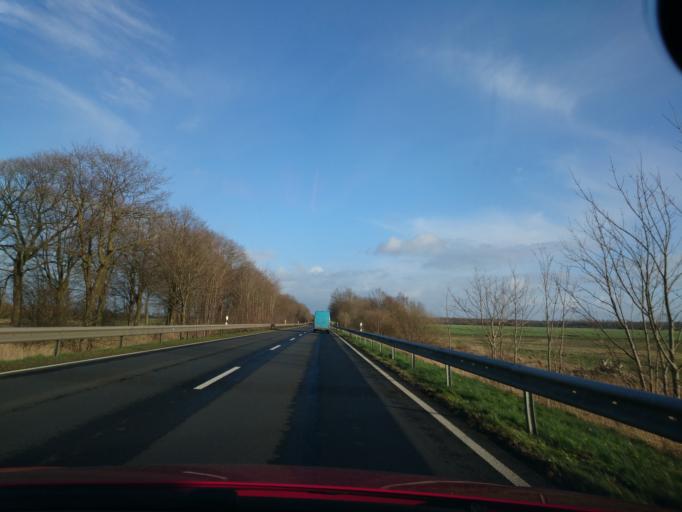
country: DE
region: Mecklenburg-Vorpommern
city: Mesekenhagen
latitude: 54.1390
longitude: 13.3342
